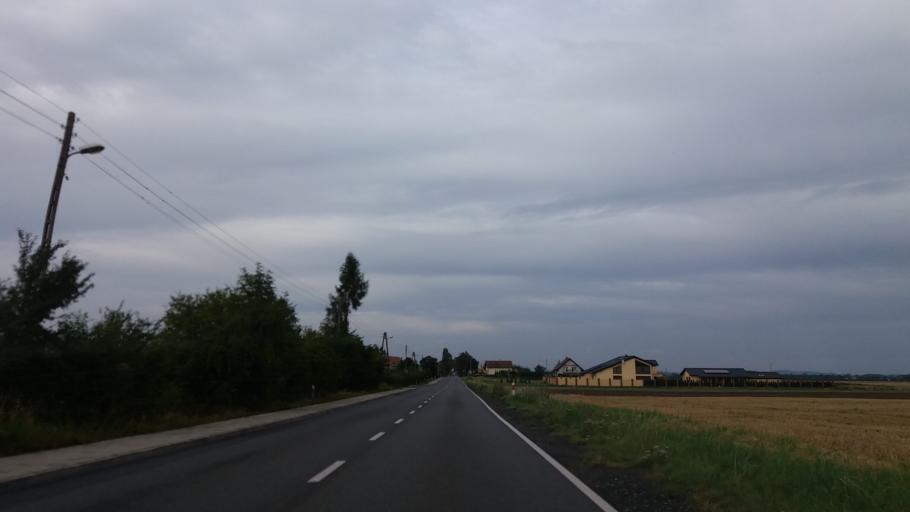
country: PL
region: Lower Silesian Voivodeship
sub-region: Powiat swidnicki
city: Stanowice
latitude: 50.9040
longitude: 16.3570
